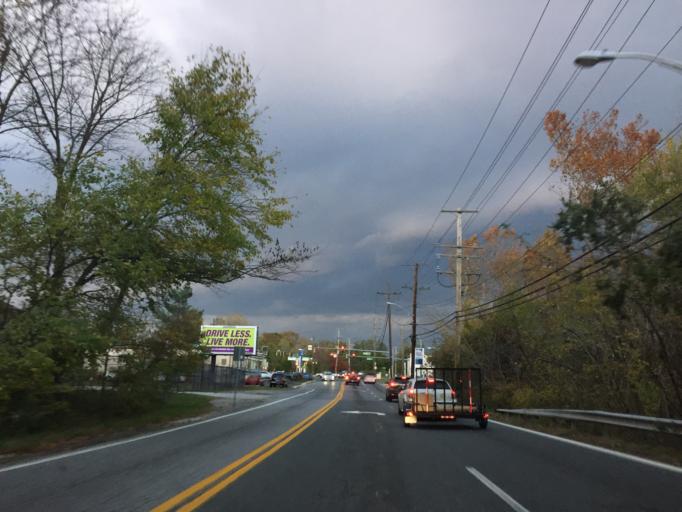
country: US
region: Maryland
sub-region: Baltimore County
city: White Marsh
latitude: 39.3795
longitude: -76.4260
